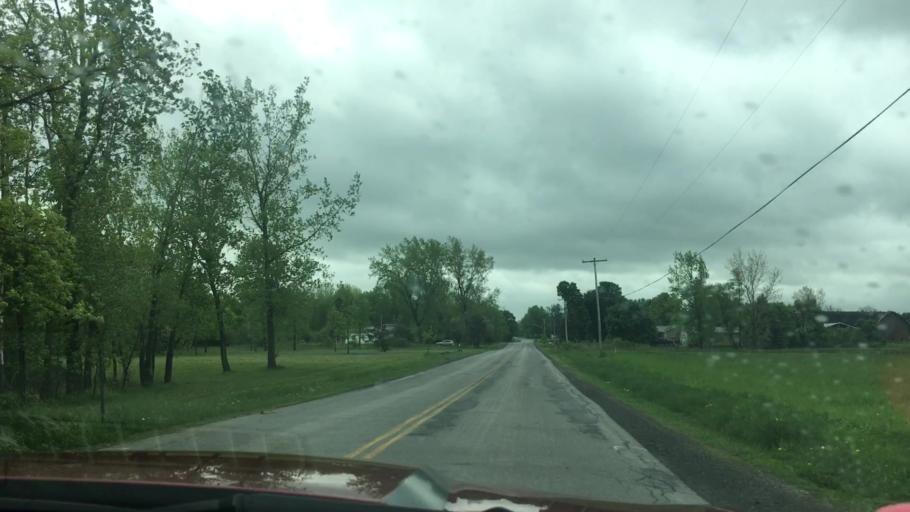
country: US
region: New York
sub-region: Genesee County
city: Batavia
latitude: 43.0777
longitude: -78.1396
